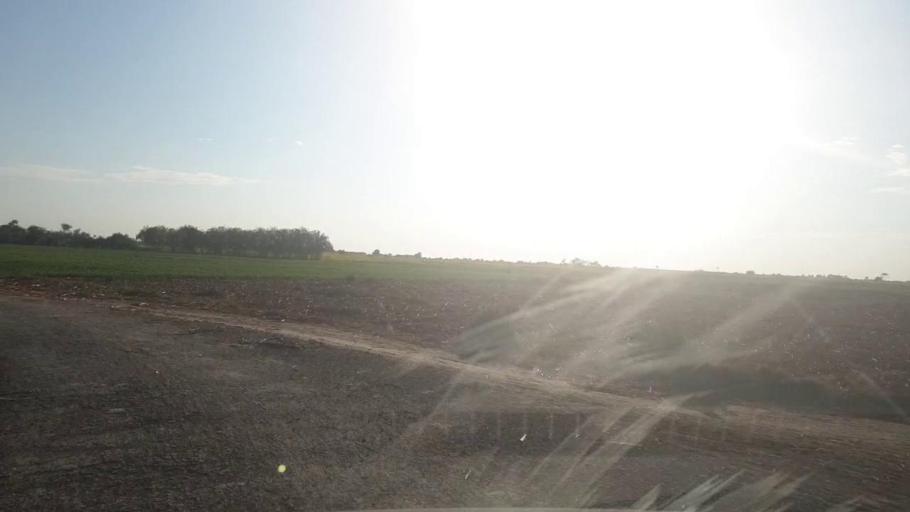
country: PK
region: Sindh
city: Sinjhoro
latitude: 26.0489
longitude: 68.8690
